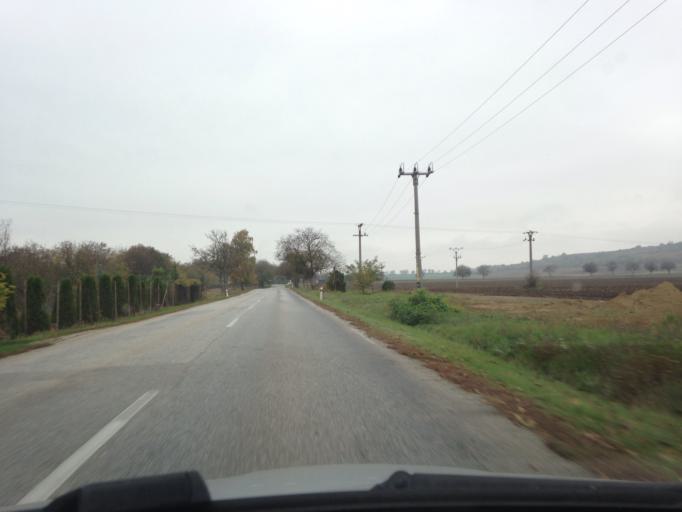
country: HU
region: Komarom-Esztergom
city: Nyergesujfalu
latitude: 47.8111
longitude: 18.6070
